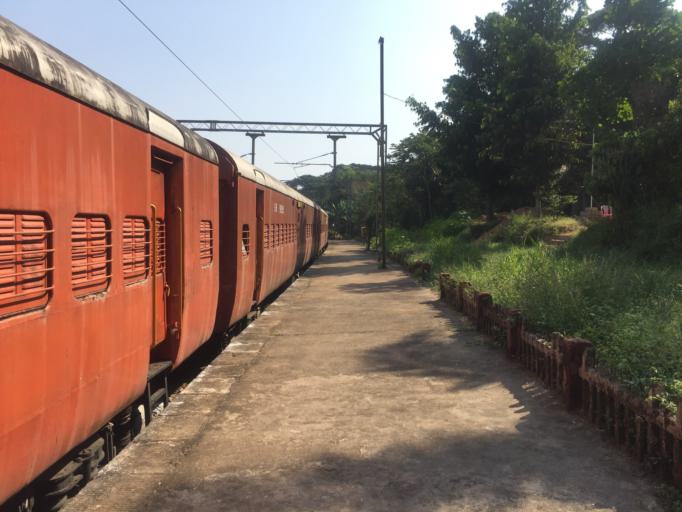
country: IN
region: Karnataka
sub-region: Dakshina Kannada
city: Ullal
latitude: 12.8617
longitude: 74.8431
